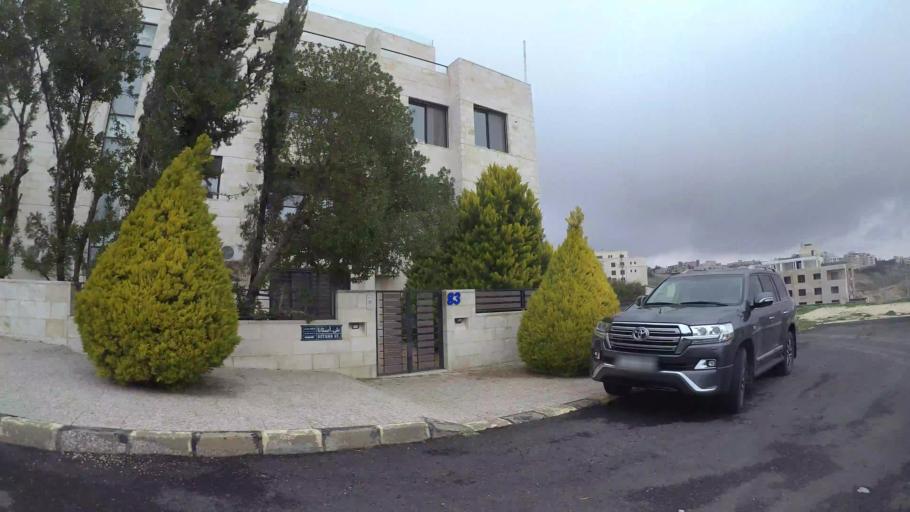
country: JO
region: Amman
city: Al Bunayyat ash Shamaliyah
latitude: 31.9327
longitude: 35.8833
